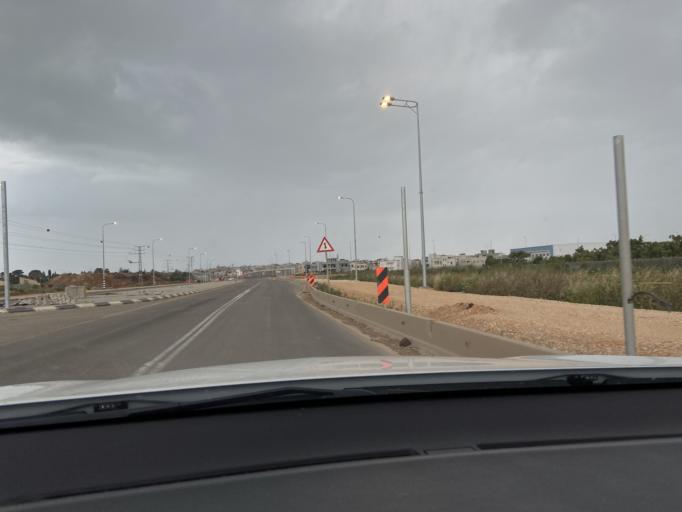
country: IL
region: Northern District
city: El Mazra`a
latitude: 32.9791
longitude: 35.1088
